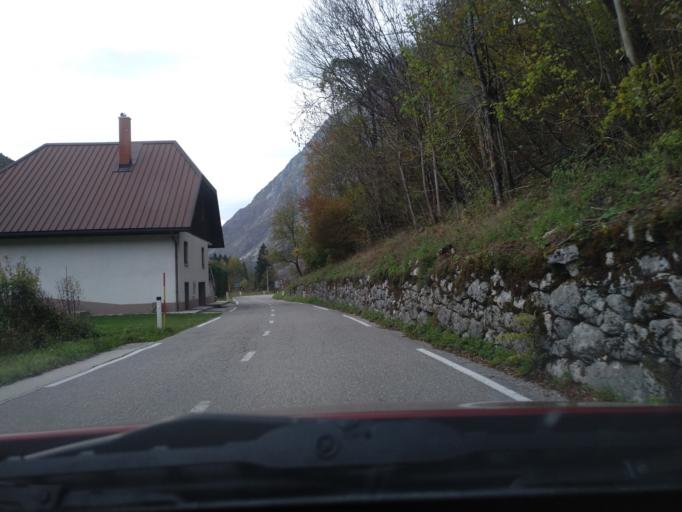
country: SI
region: Bovec
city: Bovec
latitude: 46.3407
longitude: 13.6798
